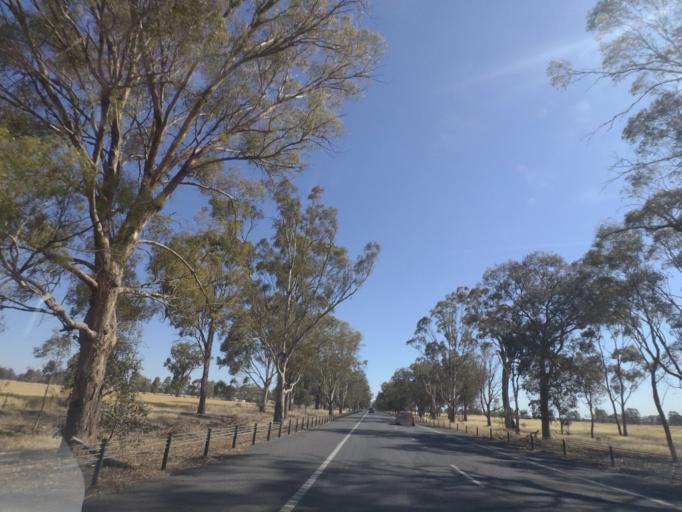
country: AU
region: Victoria
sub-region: Greater Shepparton
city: Shepparton
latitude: -36.5760
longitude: 145.3413
